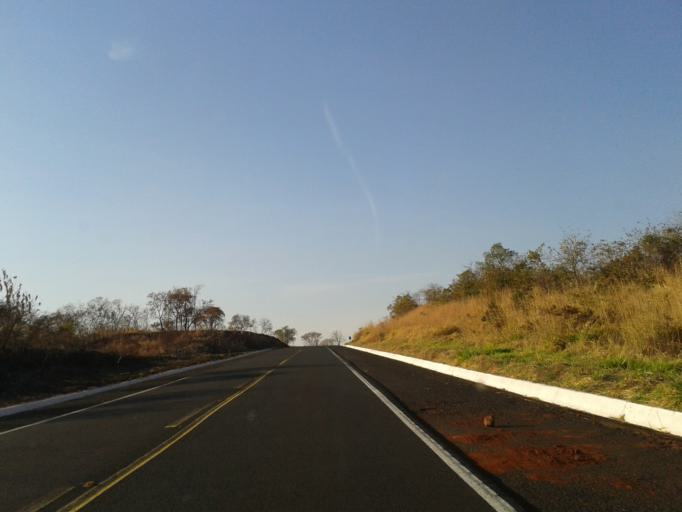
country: BR
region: Minas Gerais
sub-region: Santa Vitoria
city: Santa Vitoria
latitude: -19.1884
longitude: -50.0354
